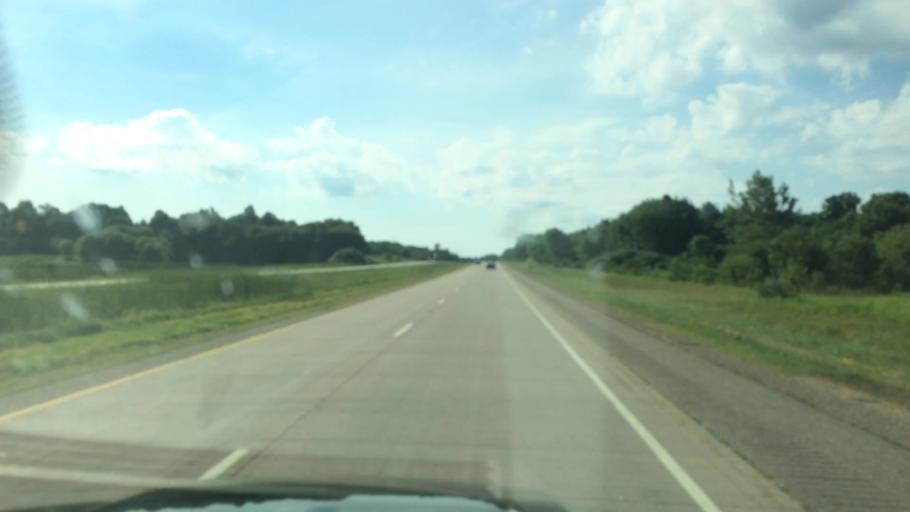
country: US
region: Wisconsin
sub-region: Shawano County
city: Wittenberg
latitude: 44.8138
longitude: -89.0461
